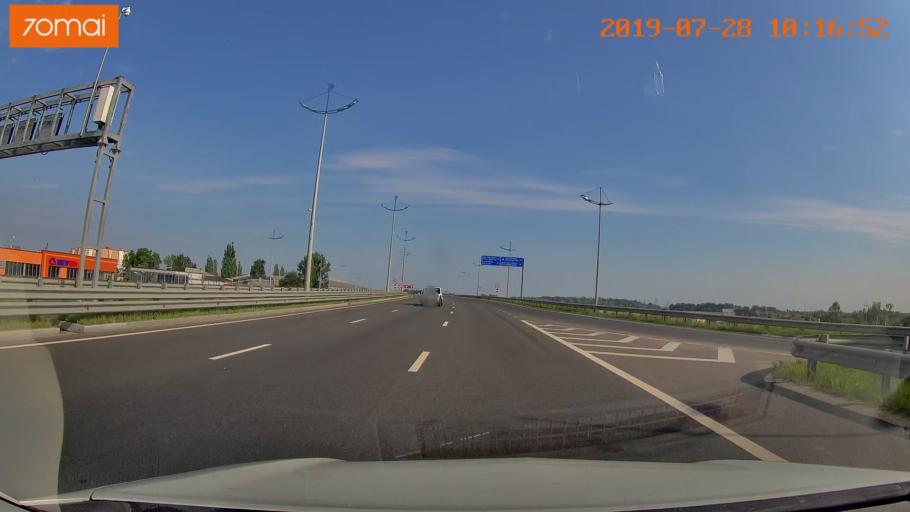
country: RU
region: Kaliningrad
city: Maloye Isakovo
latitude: 54.7320
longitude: 20.5977
